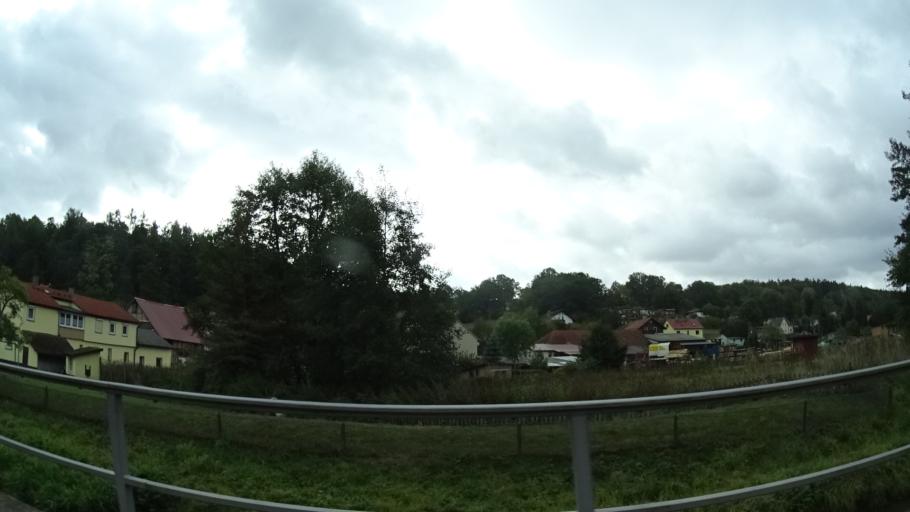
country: DE
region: Thuringia
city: Mehmels
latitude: 50.6333
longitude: 10.3336
